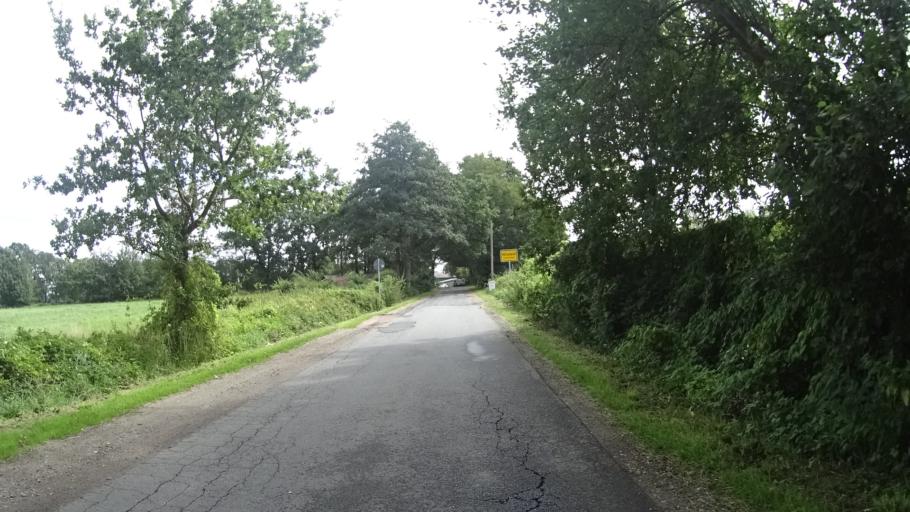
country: DE
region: Schleswig-Holstein
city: Tangstedt
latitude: 53.7533
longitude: 10.0585
